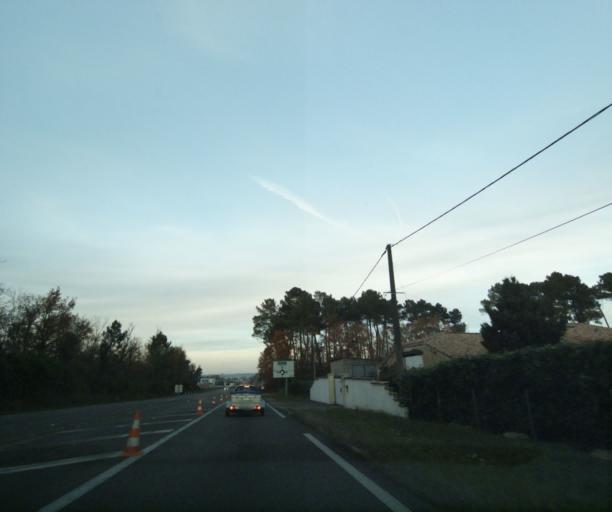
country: FR
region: Aquitaine
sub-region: Departement de la Gironde
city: Langon
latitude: 44.5139
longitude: -0.2392
